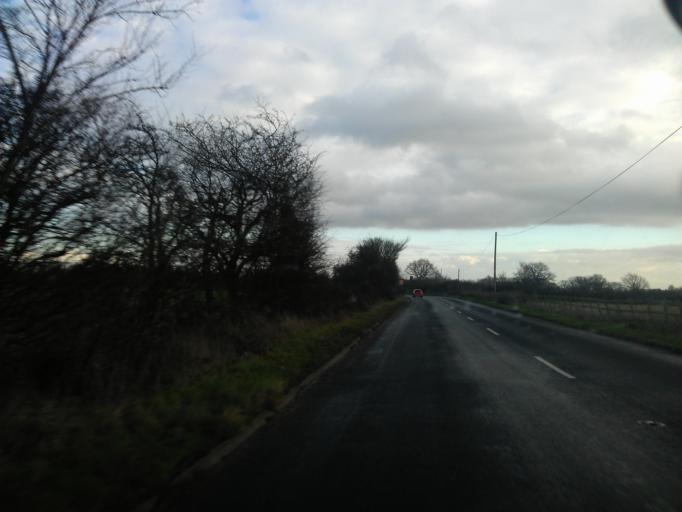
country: GB
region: England
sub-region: Essex
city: Alresford
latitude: 51.8809
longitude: 1.0223
